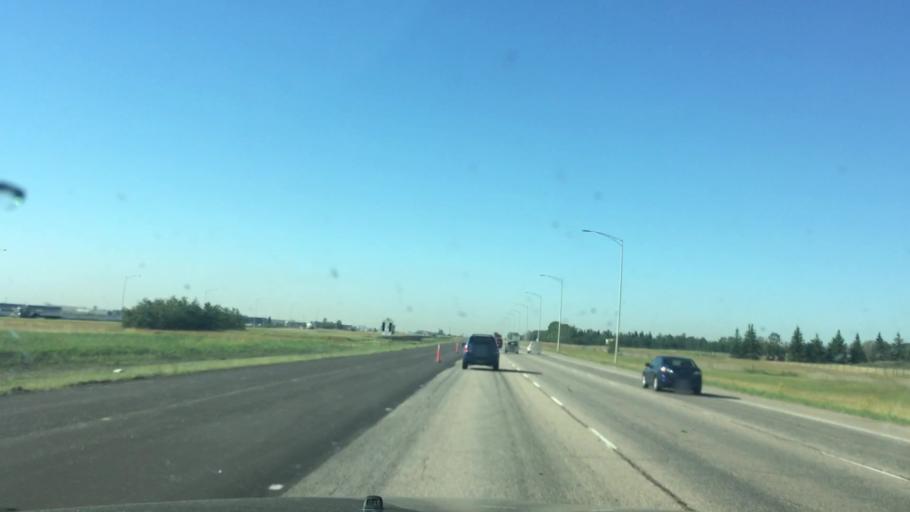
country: CA
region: Alberta
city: Beaumont
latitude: 53.3799
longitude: -113.5215
